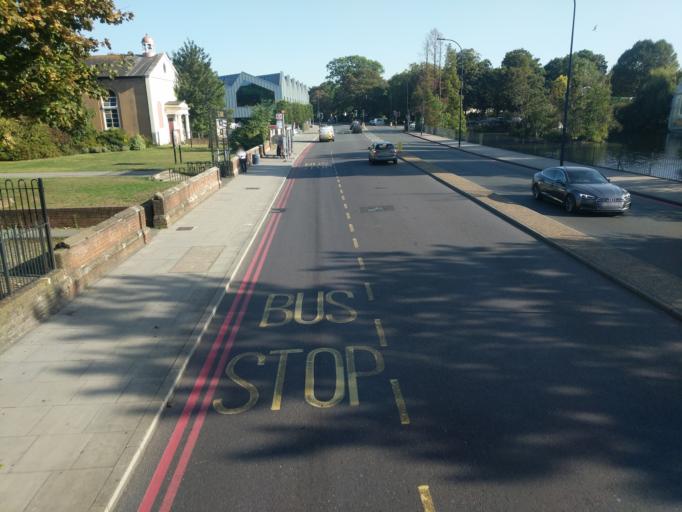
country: GB
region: England
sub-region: Greater London
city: Catford
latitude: 51.4282
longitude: -0.0122
